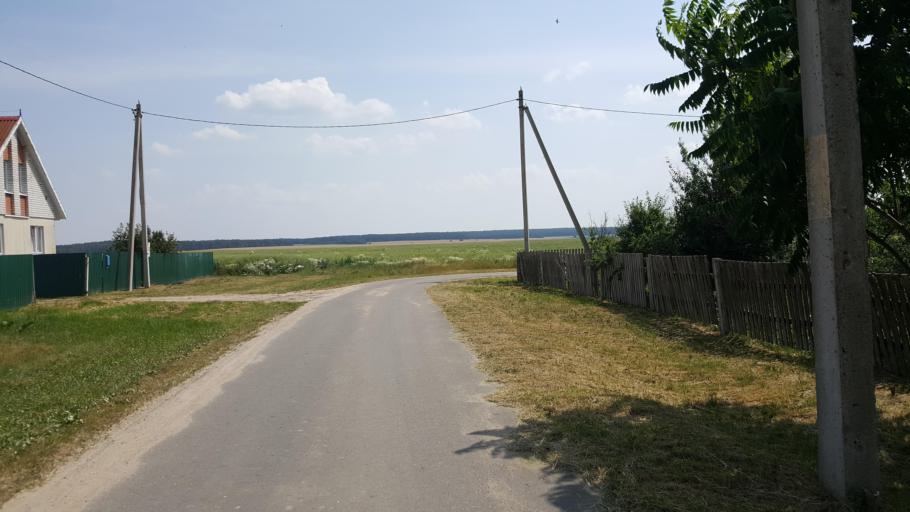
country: BY
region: Brest
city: Kamyanyets
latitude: 52.3219
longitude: 23.7851
